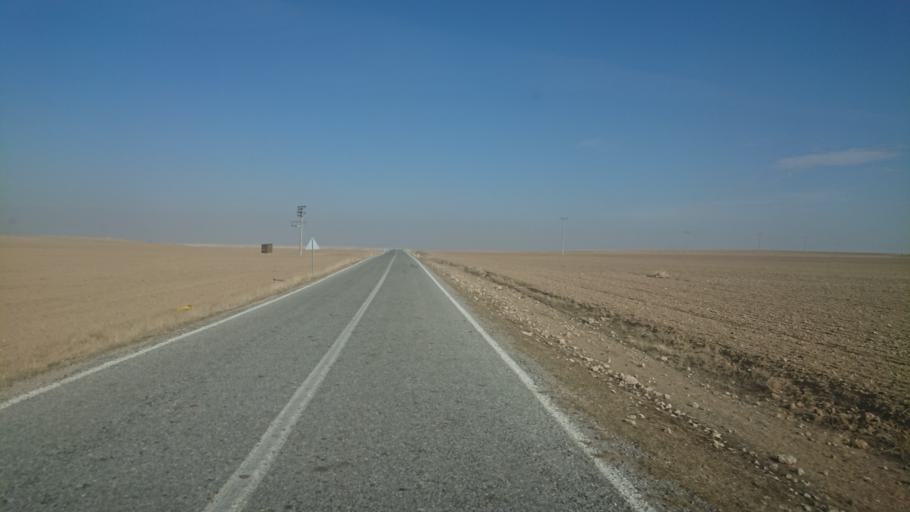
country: TR
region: Aksaray
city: Sultanhani
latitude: 38.0320
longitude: 33.5722
